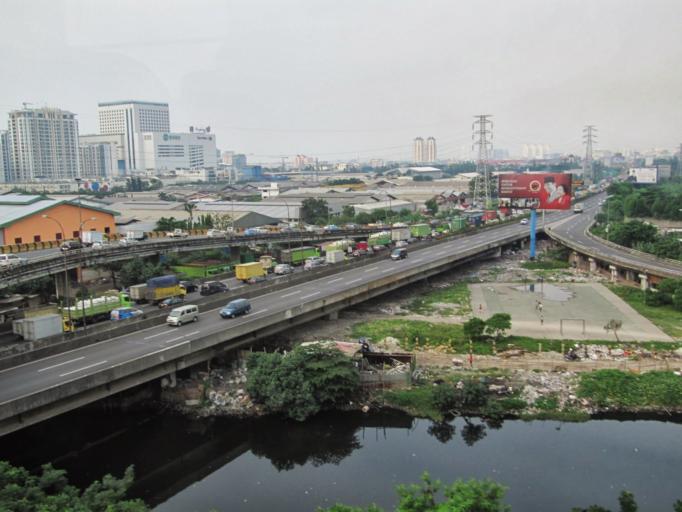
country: ID
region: Jakarta Raya
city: Jakarta
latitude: -6.1324
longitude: 106.7849
